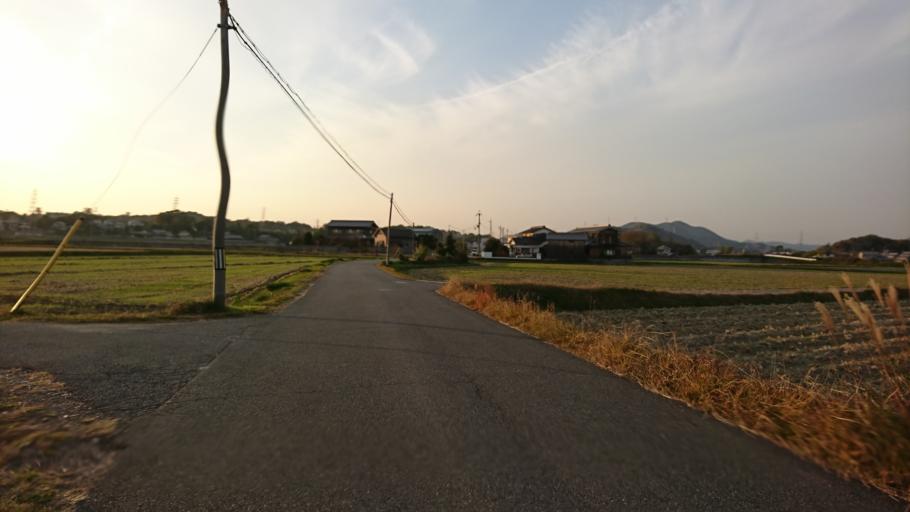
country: JP
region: Hyogo
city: Kakogawacho-honmachi
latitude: 34.7792
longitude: 134.8746
